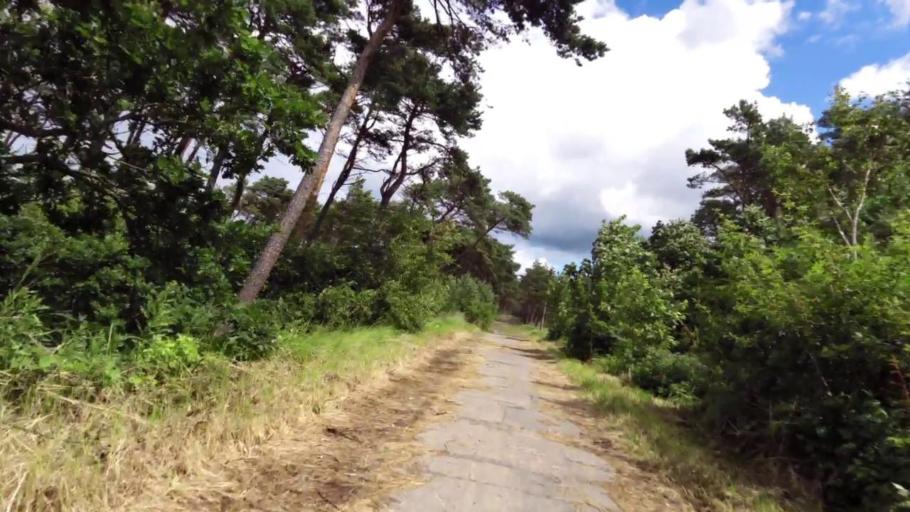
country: PL
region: West Pomeranian Voivodeship
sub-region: Powiat slawienski
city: Darlowo
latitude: 54.4959
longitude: 16.4476
